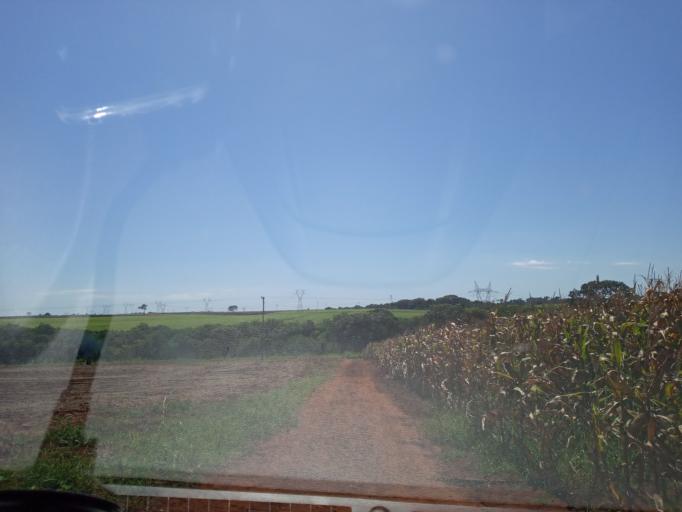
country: BR
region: Goias
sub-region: Itumbiara
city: Itumbiara
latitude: -18.4449
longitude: -49.1443
